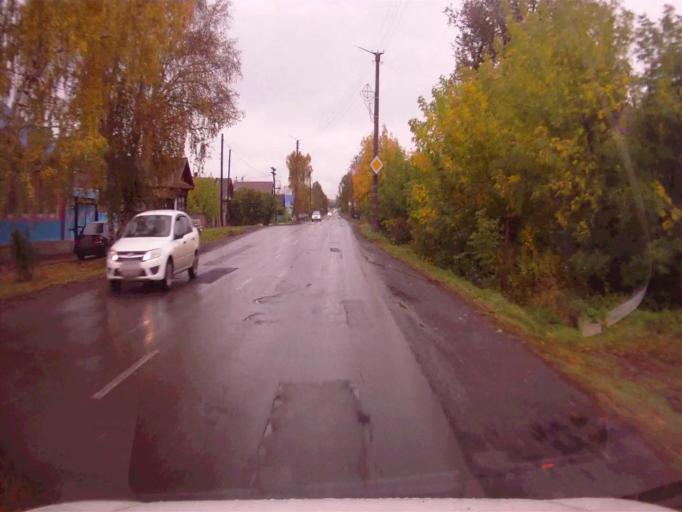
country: RU
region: Chelyabinsk
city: Verkhniy Ufaley
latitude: 56.0509
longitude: 60.2353
